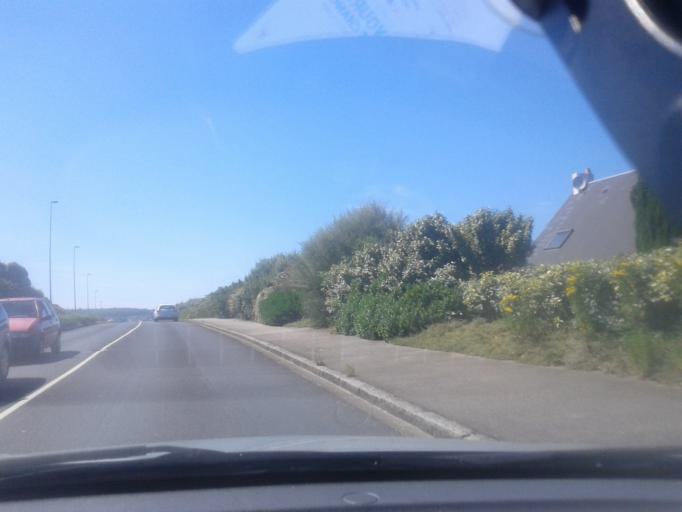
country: FR
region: Lower Normandy
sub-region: Departement de la Manche
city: Equeurdreville-Hainneville
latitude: 49.6534
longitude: -1.6635
